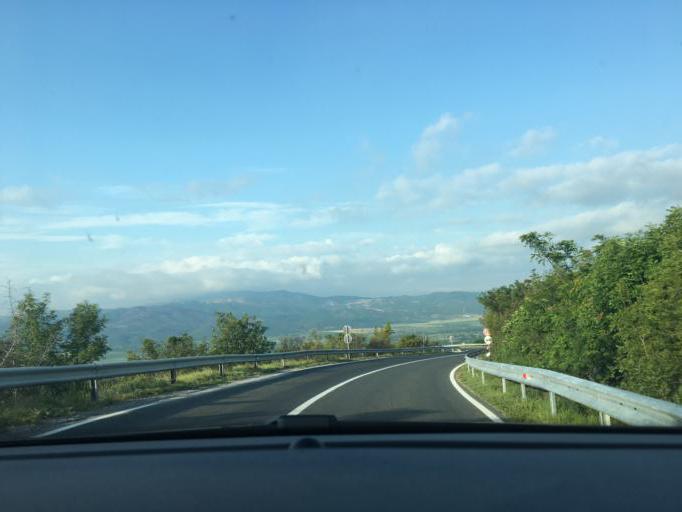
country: MK
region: Valandovo
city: Valandovo
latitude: 41.3259
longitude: 22.5974
